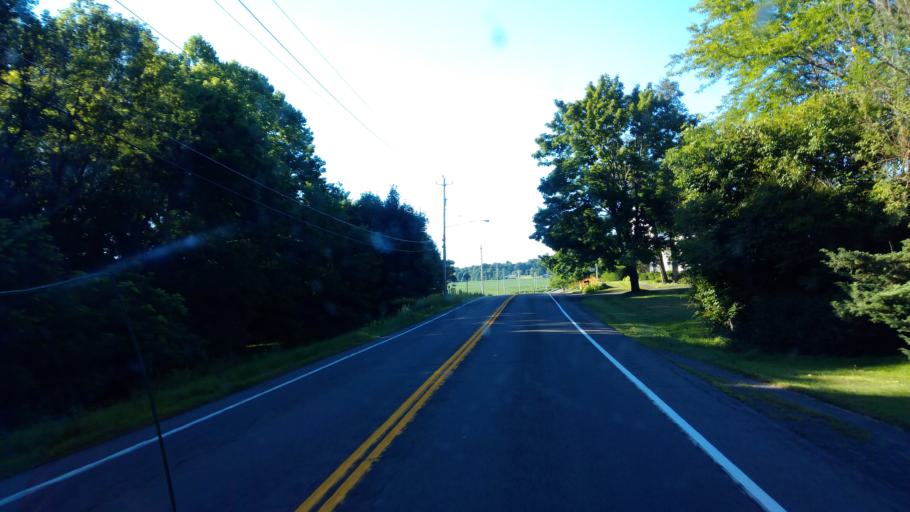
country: US
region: New York
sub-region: Wayne County
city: Lyons
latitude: 43.0229
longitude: -76.9882
